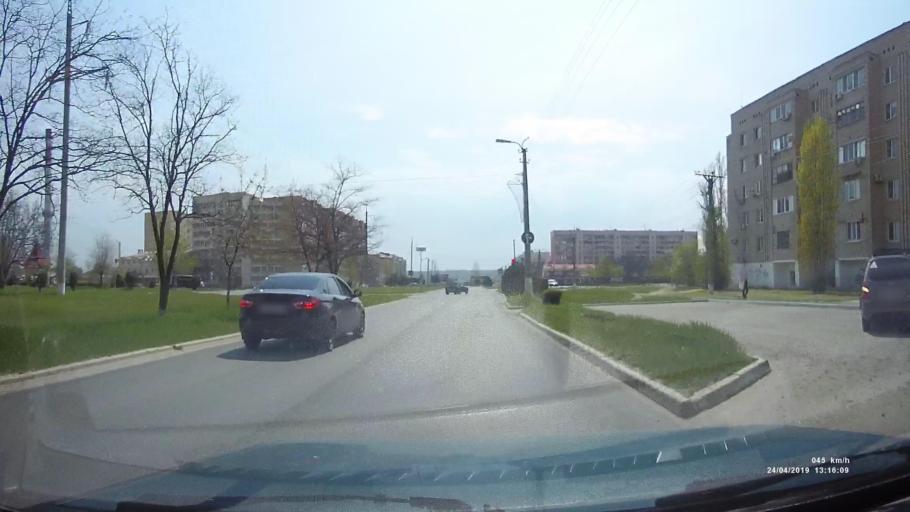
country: RU
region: Kalmykiya
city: Elista
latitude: 46.3056
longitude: 44.3044
